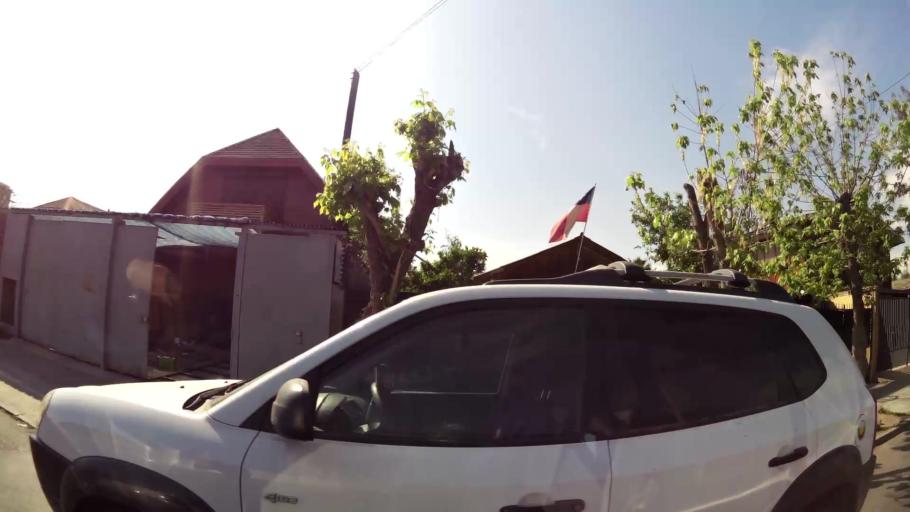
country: CL
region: Santiago Metropolitan
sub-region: Provincia de Santiago
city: La Pintana
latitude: -33.5474
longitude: -70.5935
